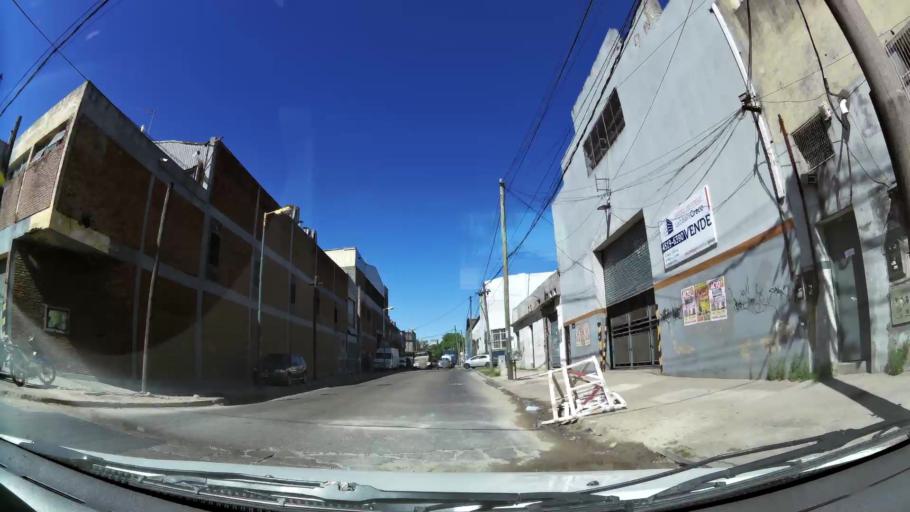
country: AR
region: Buenos Aires
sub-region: Partido de General San Martin
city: General San Martin
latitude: -34.5572
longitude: -58.5232
